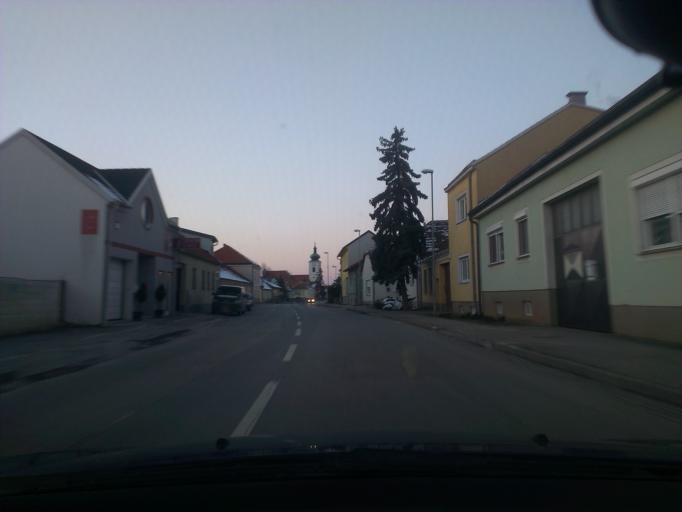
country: AT
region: Lower Austria
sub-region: Politischer Bezirk Bruck an der Leitha
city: Enzersdorf an der Fischa
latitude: 48.0813
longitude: 16.6066
